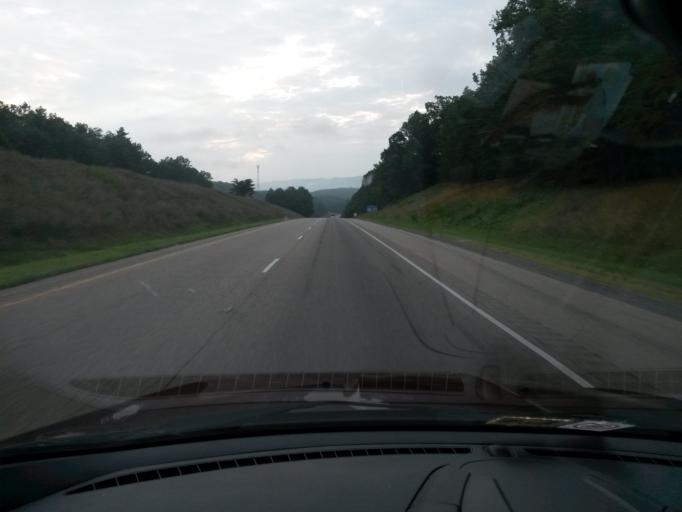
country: US
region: Virginia
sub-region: Alleghany County
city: Clifton Forge
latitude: 37.8288
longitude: -79.7761
